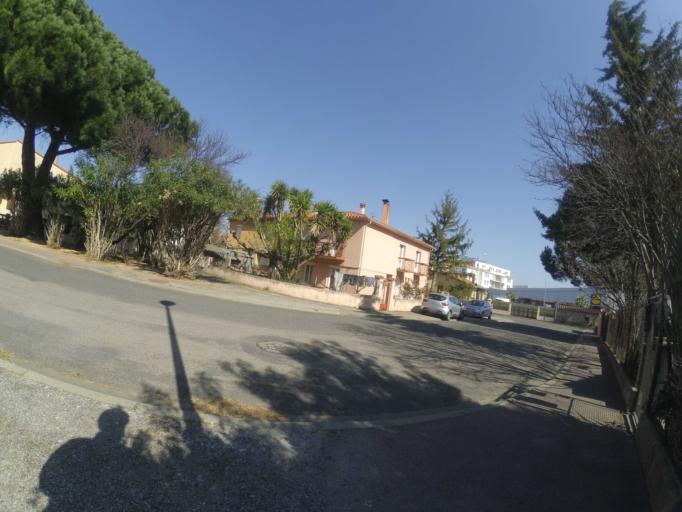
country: FR
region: Languedoc-Roussillon
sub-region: Departement des Pyrenees-Orientales
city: Thuir
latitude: 42.6286
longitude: 2.7605
